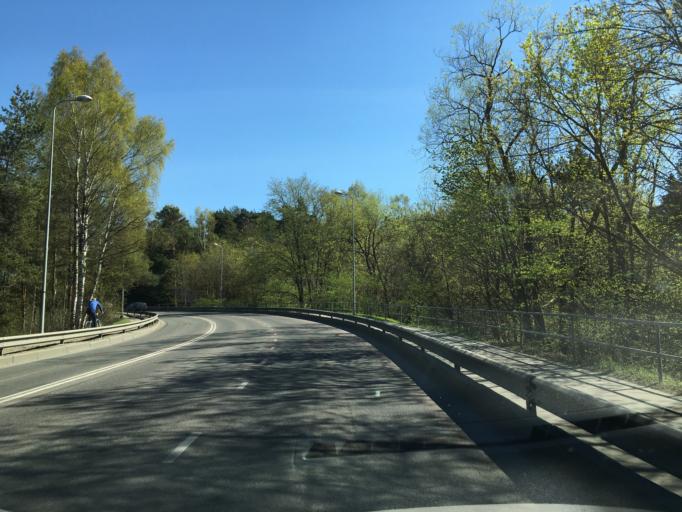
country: EE
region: Harju
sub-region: Saue vald
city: Laagri
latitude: 59.3908
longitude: 24.6796
